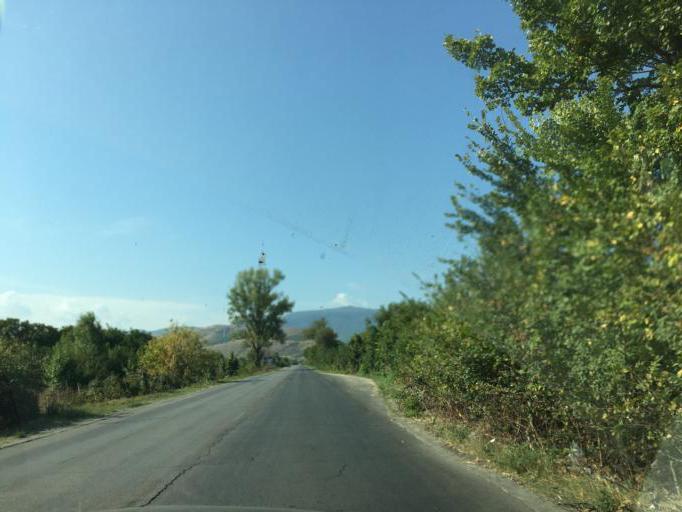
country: BG
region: Pazardzhik
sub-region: Obshtina Pazardzhik
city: Pazardzhik
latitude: 42.1425
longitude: 24.3016
